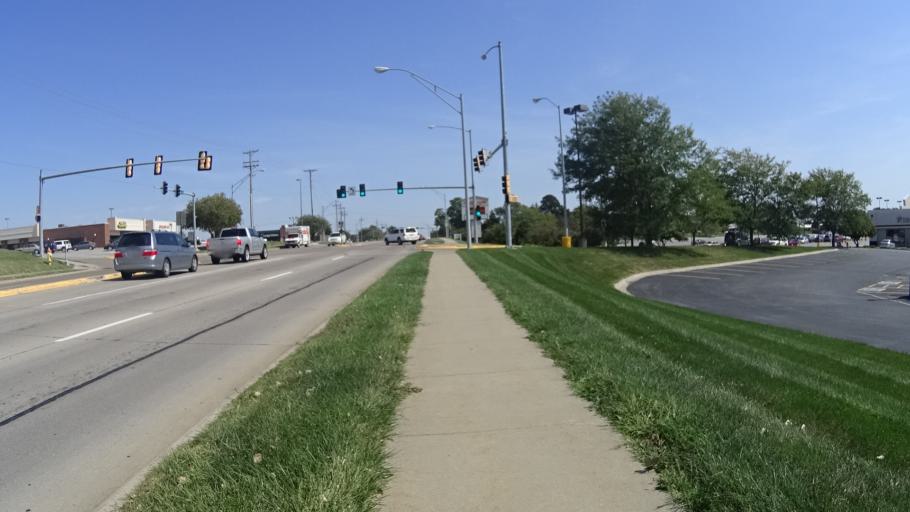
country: US
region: Nebraska
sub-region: Sarpy County
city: La Vista
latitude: 41.1761
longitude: -96.0459
